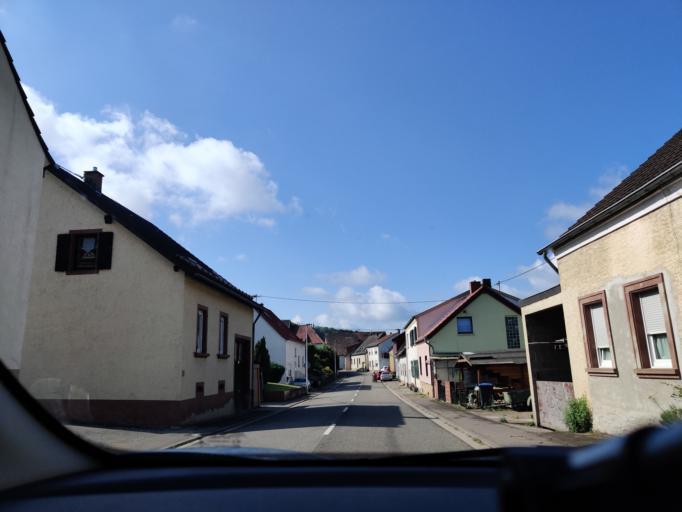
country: DE
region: Saarland
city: Gersheim
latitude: 49.1688
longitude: 7.1615
